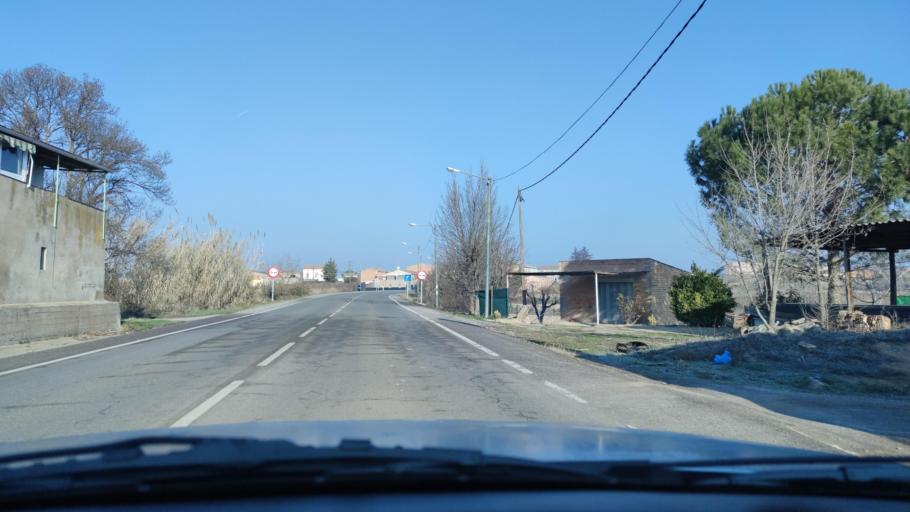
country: ES
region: Catalonia
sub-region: Provincia de Lleida
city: Lleida
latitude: 41.6417
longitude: 0.6360
